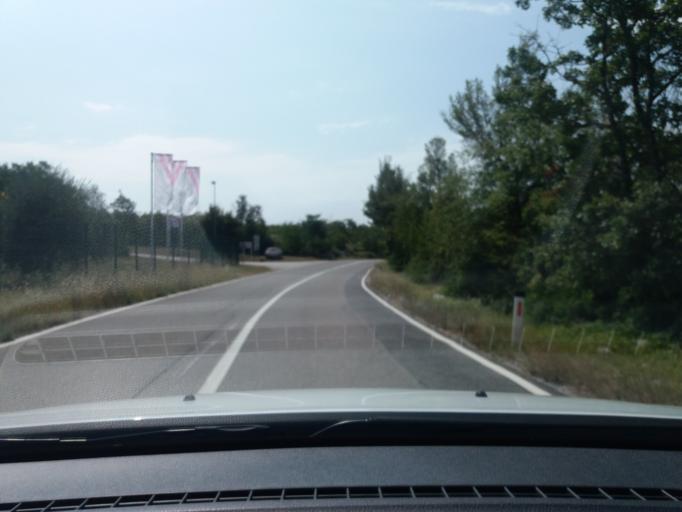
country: SI
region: Miren-Kostanjevica
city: Miren
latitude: 45.8592
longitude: 13.5860
